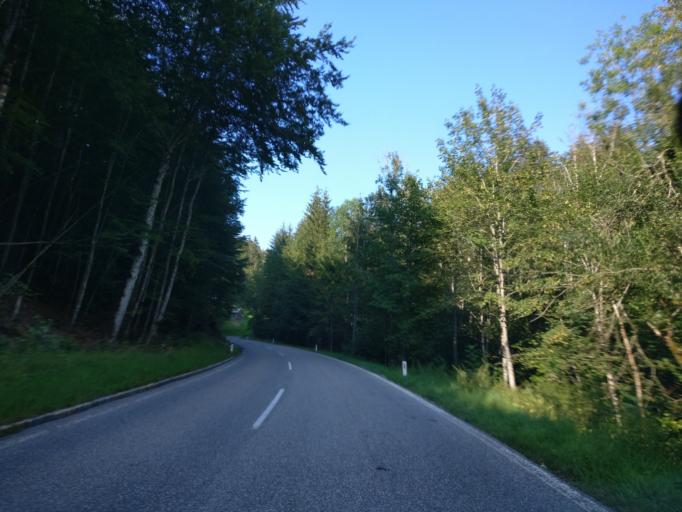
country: AT
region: Lower Austria
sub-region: Politischer Bezirk Scheibbs
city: Gostling an der Ybbs
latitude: 47.7405
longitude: 14.8904
